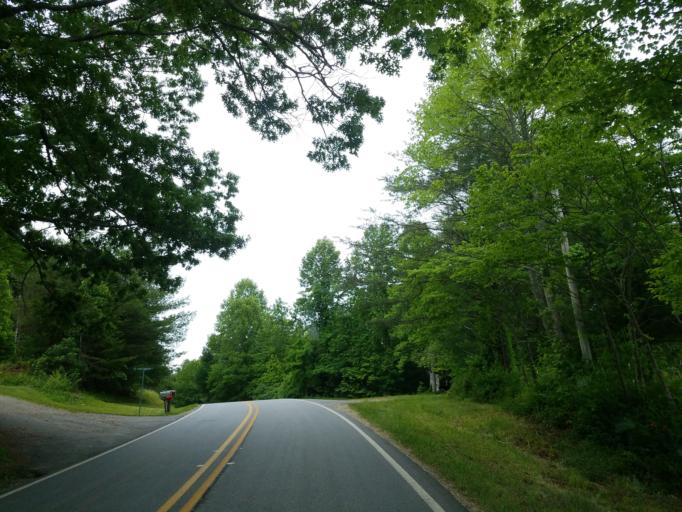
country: US
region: Georgia
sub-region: Lumpkin County
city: Dahlonega
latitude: 34.6908
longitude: -84.0193
